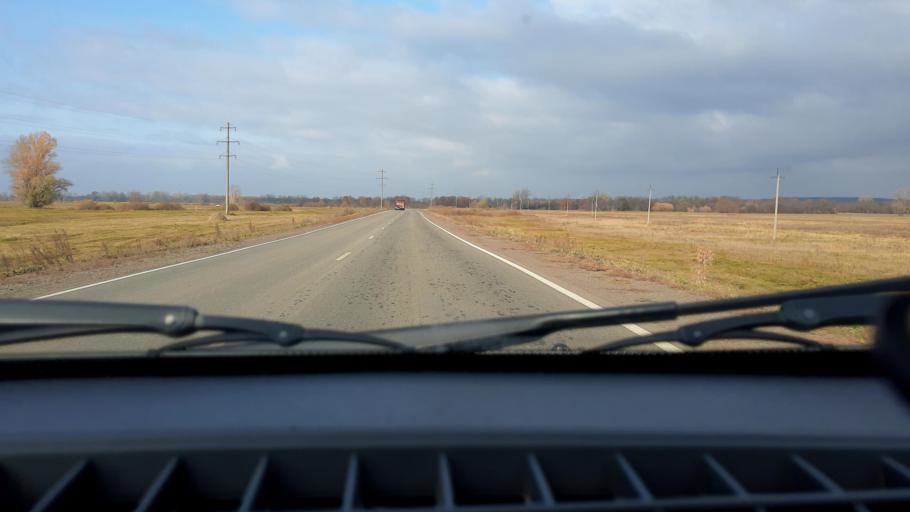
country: RU
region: Bashkortostan
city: Kabakovo
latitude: 54.5598
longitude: 56.0070
